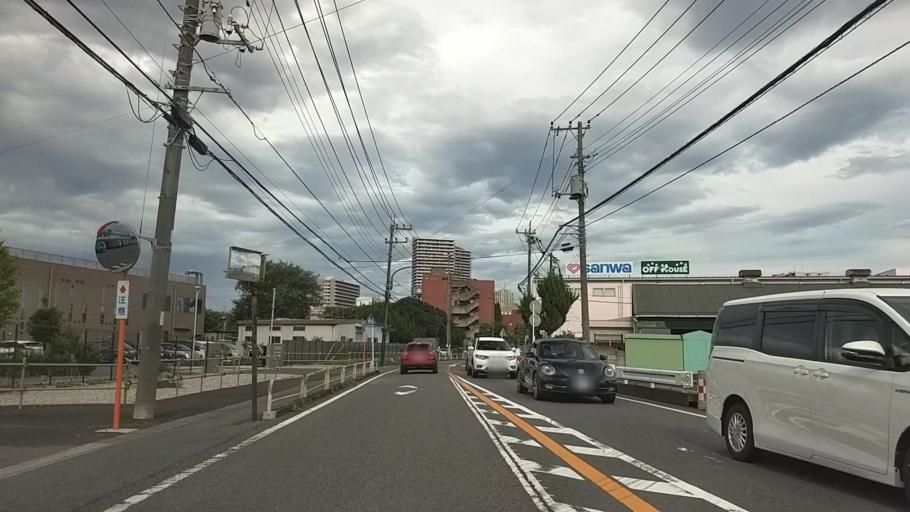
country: JP
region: Tokyo
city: Hachioji
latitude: 35.5952
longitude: 139.3291
